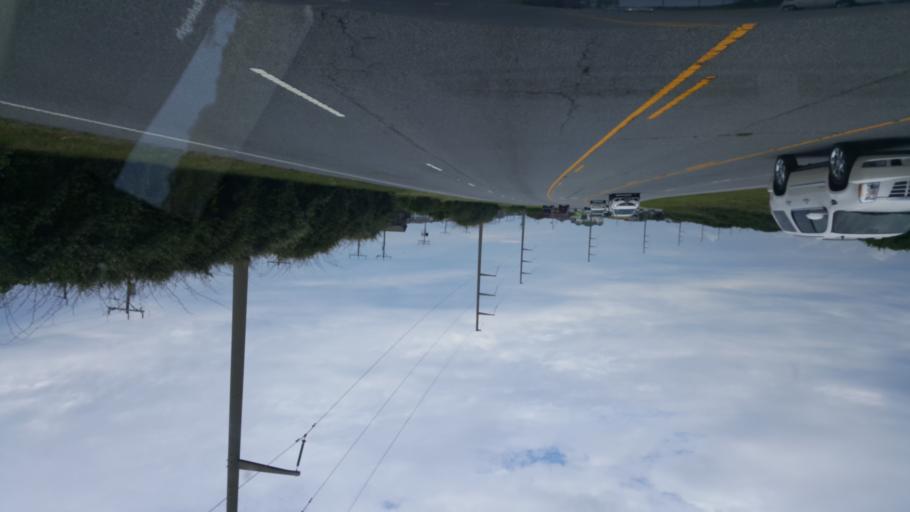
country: US
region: North Carolina
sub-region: Dare County
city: Nags Head
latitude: 35.9613
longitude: -75.6267
